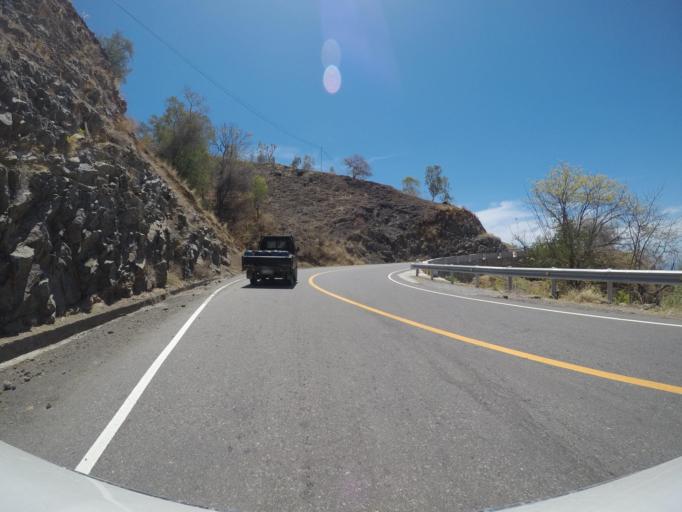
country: TL
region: Manatuto
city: Manatuto
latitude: -8.4914
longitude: 125.9543
